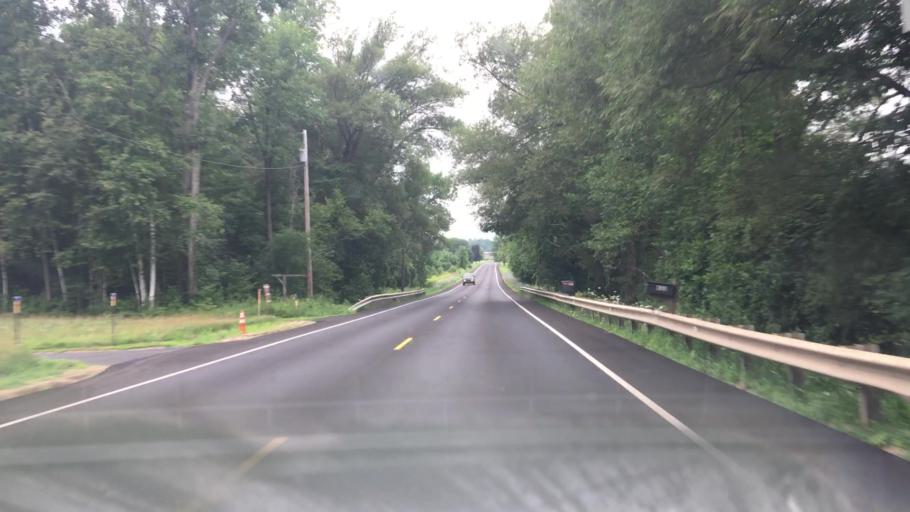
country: US
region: New York
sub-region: Clinton County
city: Morrisonville
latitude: 44.6490
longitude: -73.5595
